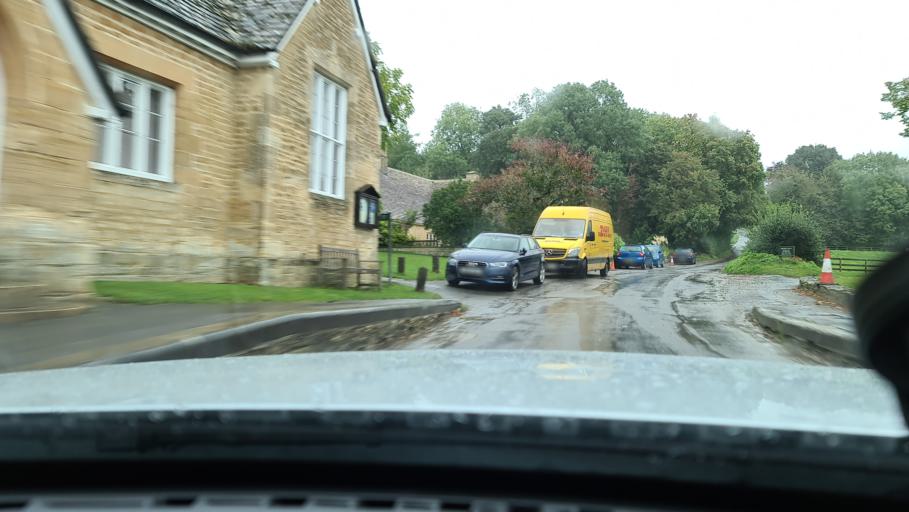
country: GB
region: England
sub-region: Oxfordshire
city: Woodstock
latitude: 51.8915
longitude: -1.3815
